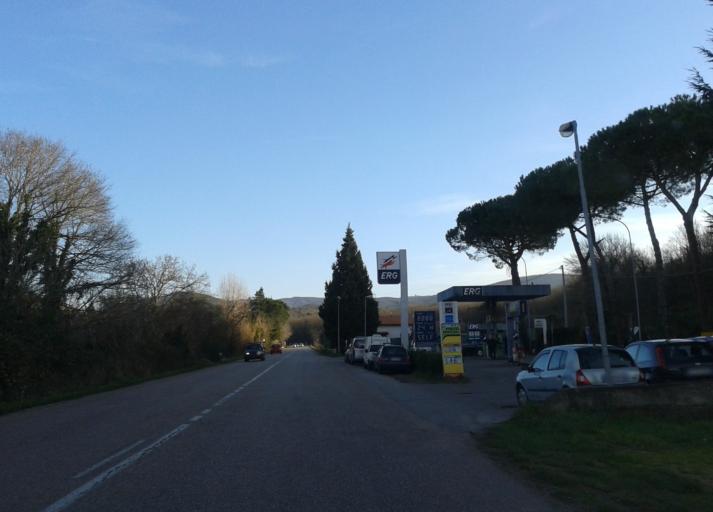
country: IT
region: Tuscany
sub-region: Provincia di Livorno
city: Guasticce
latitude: 43.5699
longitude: 10.3781
